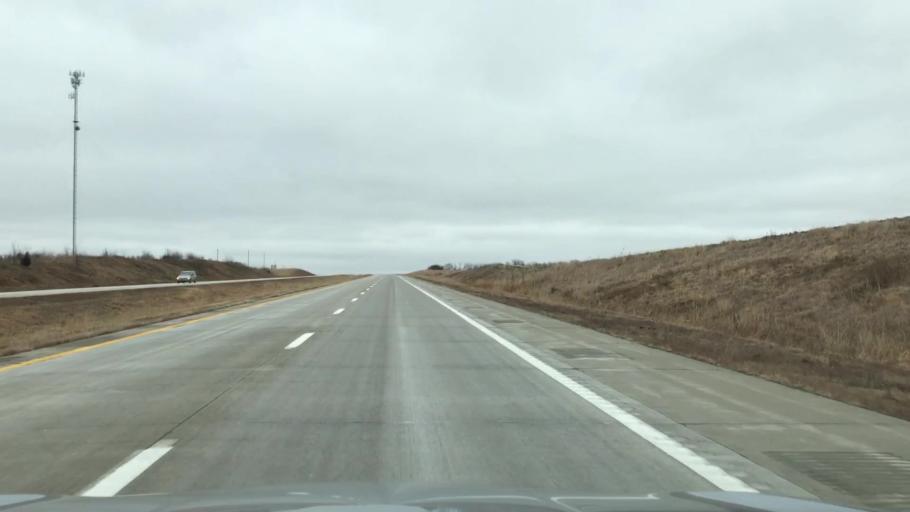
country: US
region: Missouri
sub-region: Caldwell County
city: Hamilton
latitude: 39.7348
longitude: -93.7728
